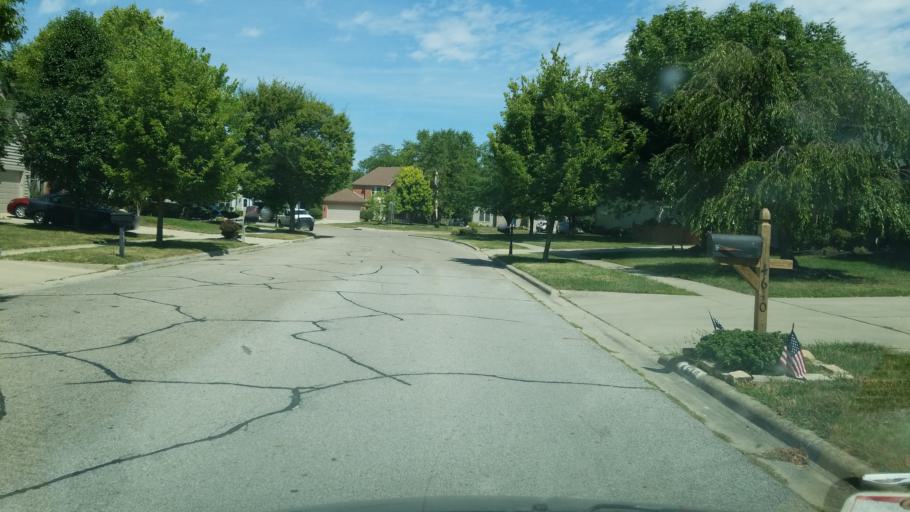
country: US
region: Ohio
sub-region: Franklin County
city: Grove City
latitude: 39.8699
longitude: -83.0887
